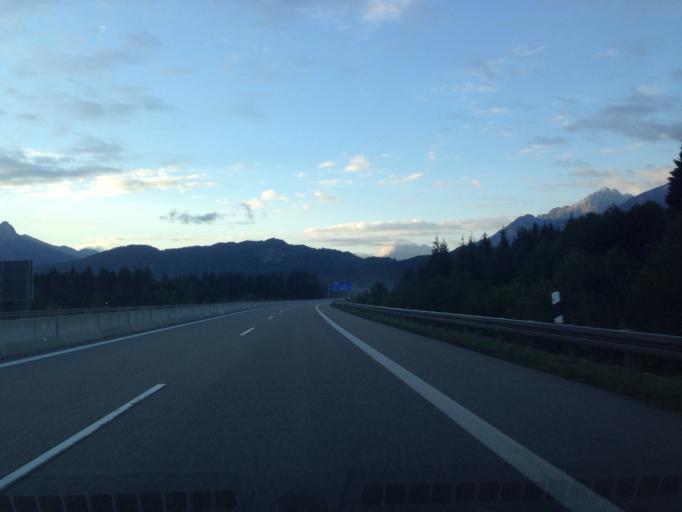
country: DE
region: Bavaria
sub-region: Swabia
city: Hopferau
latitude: 47.5871
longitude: 10.6594
